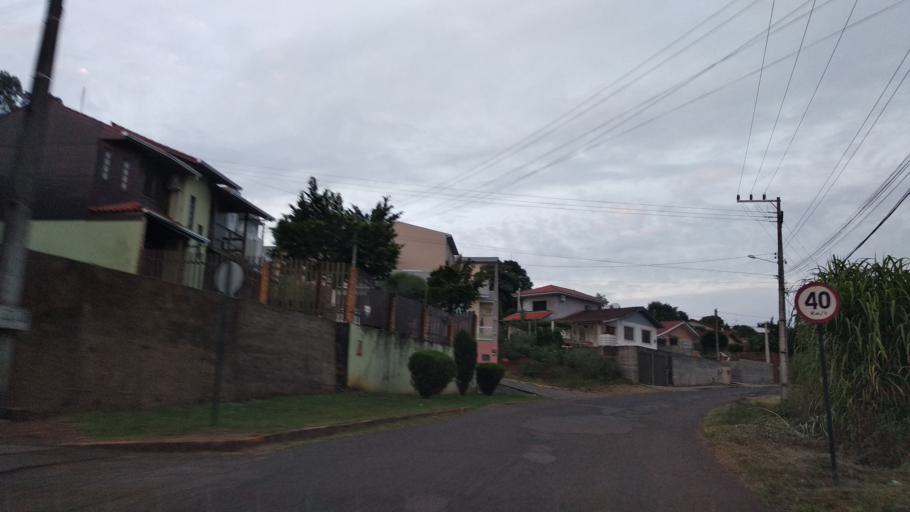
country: BR
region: Santa Catarina
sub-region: Videira
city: Videira
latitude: -26.9958
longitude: -51.1824
